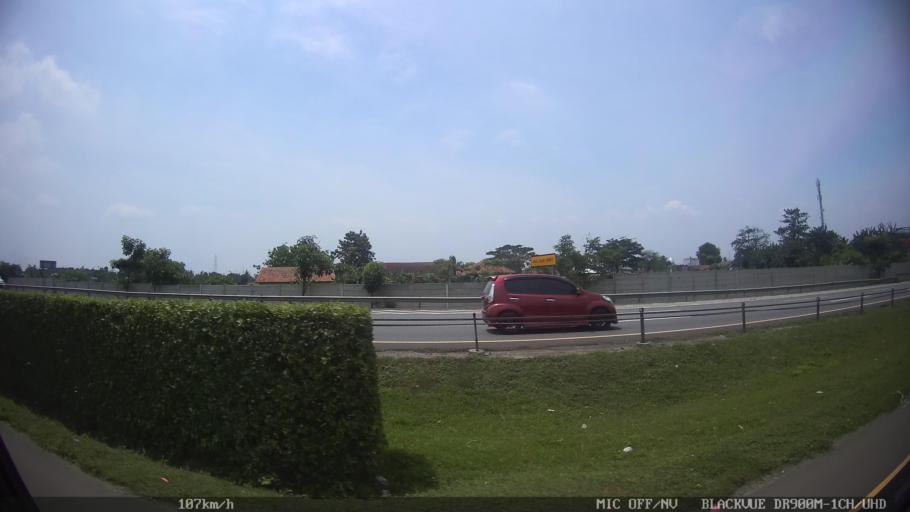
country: ID
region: West Java
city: Kresek
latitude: -6.1771
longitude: 106.3588
